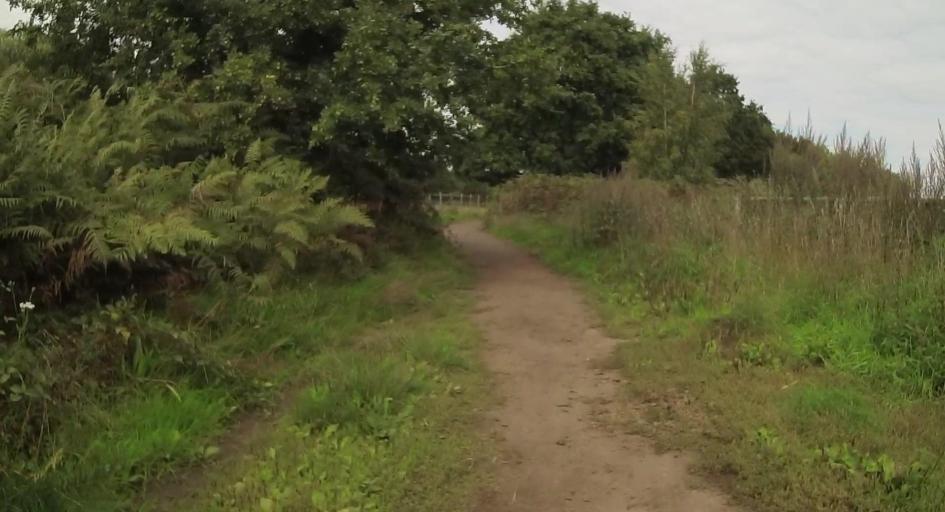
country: GB
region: England
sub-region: Surrey
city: Woking
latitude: 51.3460
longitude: -0.5644
